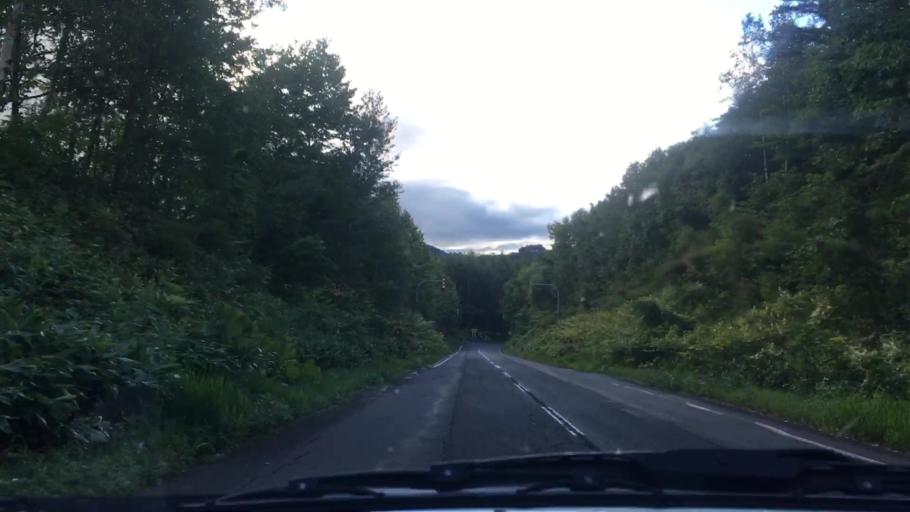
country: JP
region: Hokkaido
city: Otofuke
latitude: 43.1754
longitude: 142.9276
